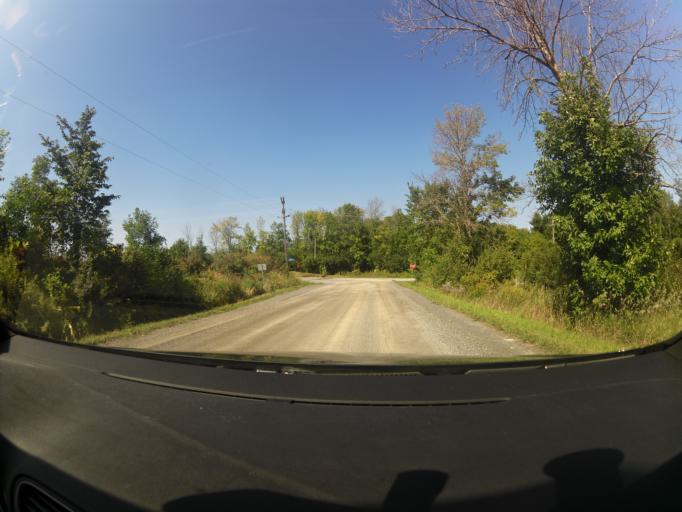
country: CA
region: Ontario
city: Arnprior
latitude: 45.3420
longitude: -76.2676
